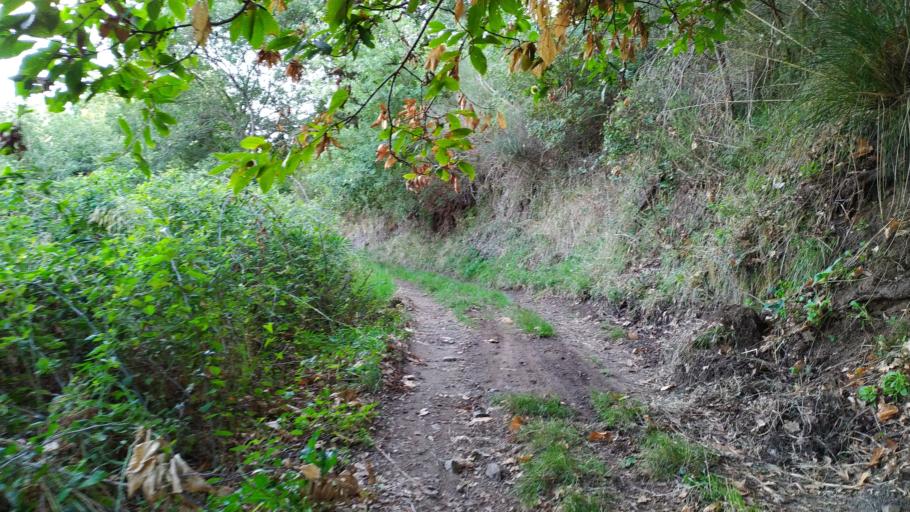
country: IT
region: Sicily
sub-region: Messina
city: Condro
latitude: 38.1627
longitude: 15.3317
